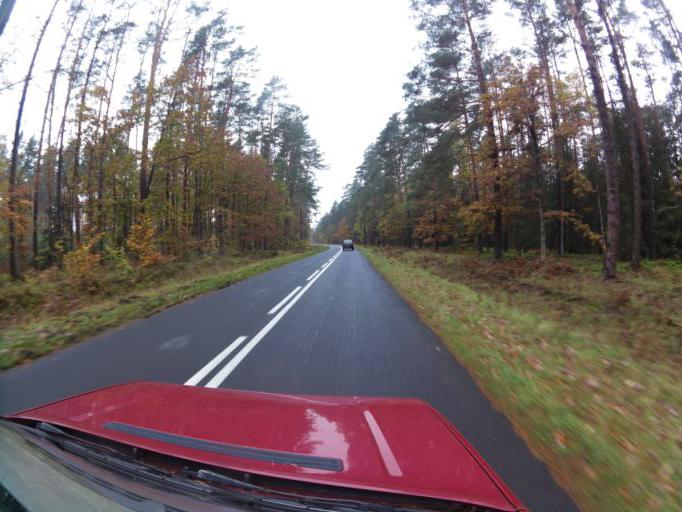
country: PL
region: West Pomeranian Voivodeship
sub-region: Powiat policki
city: Dobra
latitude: 53.5828
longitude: 14.4131
